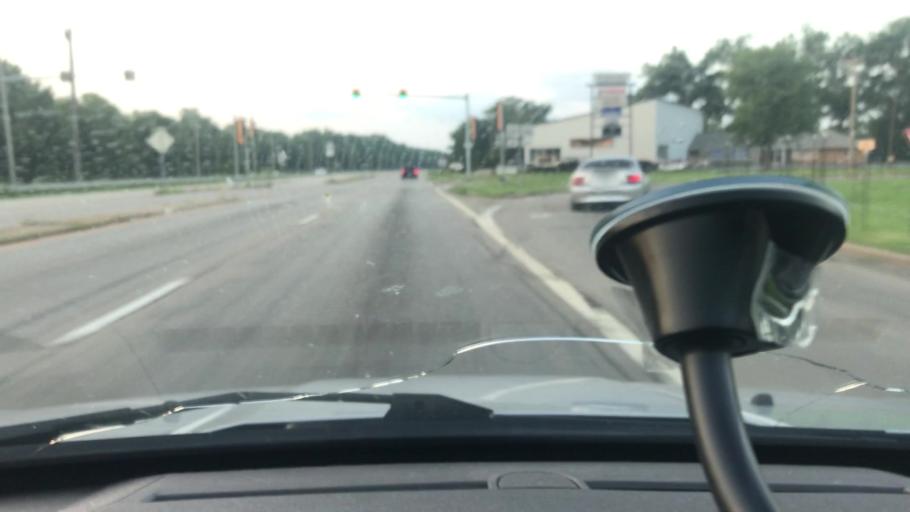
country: US
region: Illinois
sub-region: Tazewell County
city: North Pekin
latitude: 40.6037
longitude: -89.6370
